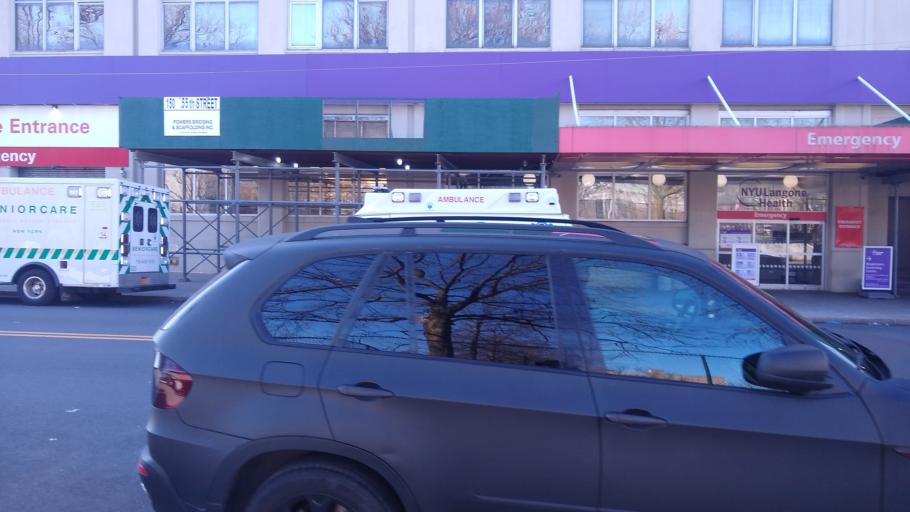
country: US
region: New York
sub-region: Kings County
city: Bensonhurst
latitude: 40.6460
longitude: -74.0200
